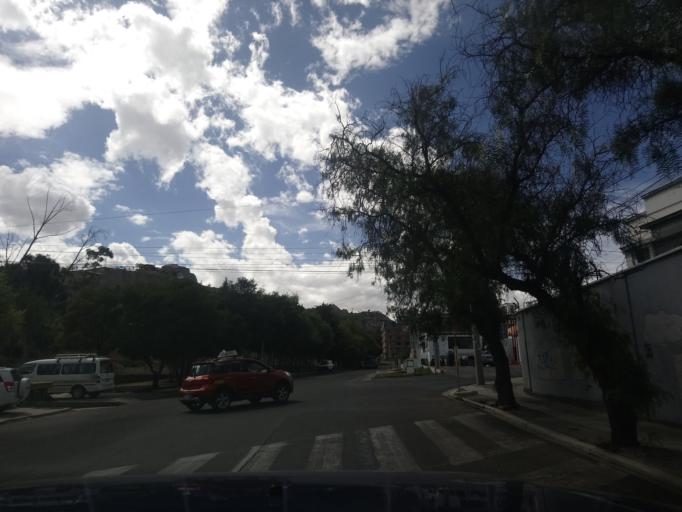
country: BO
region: La Paz
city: La Paz
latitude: -16.5270
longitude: -68.1114
